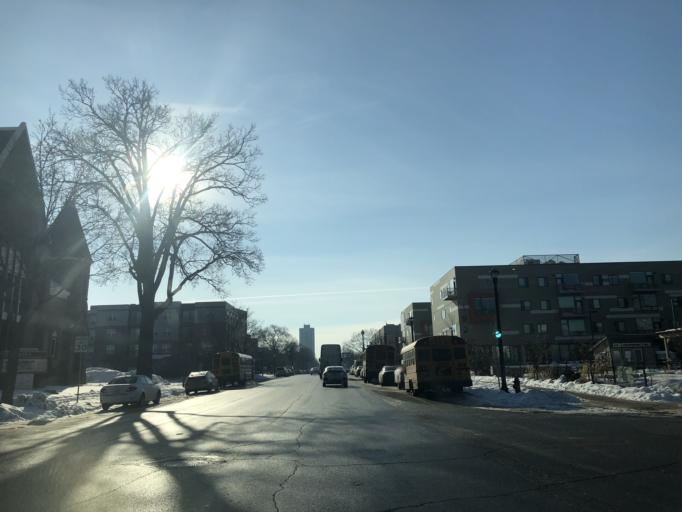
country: US
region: Minnesota
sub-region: Hennepin County
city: Minneapolis
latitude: 44.9642
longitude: -93.2677
